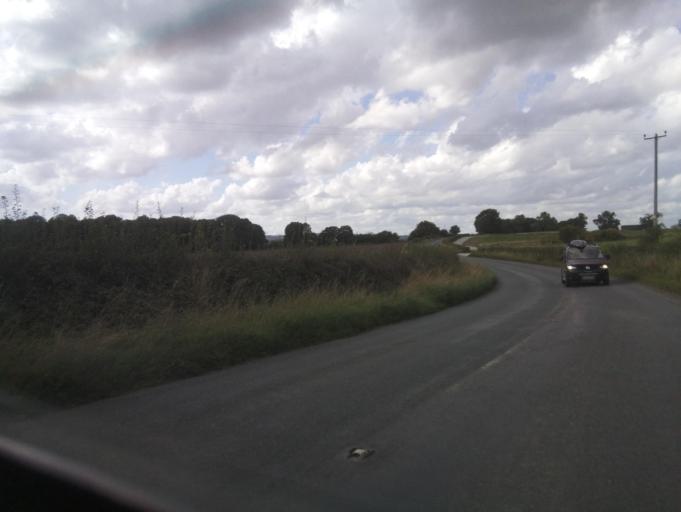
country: GB
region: England
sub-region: North Yorkshire
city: Bedale
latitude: 54.2198
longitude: -1.6335
